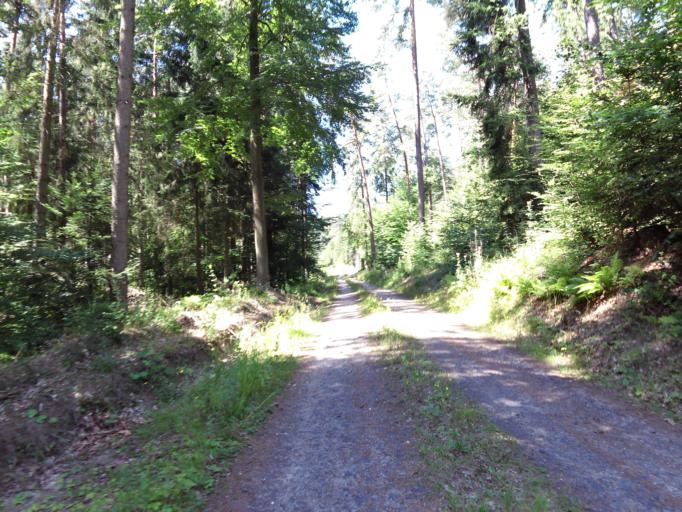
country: DE
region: Rheinland-Pfalz
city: Carlsberg
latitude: 49.4775
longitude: 8.0393
